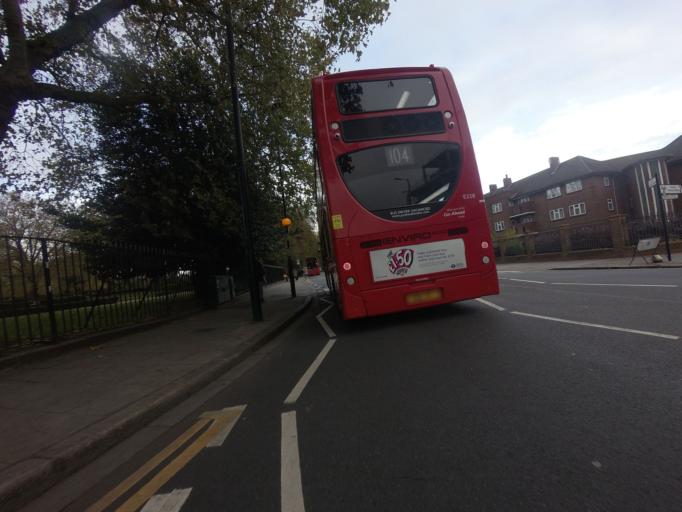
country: GB
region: England
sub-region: Greater London
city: East Ham
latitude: 51.5283
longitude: 0.0563
